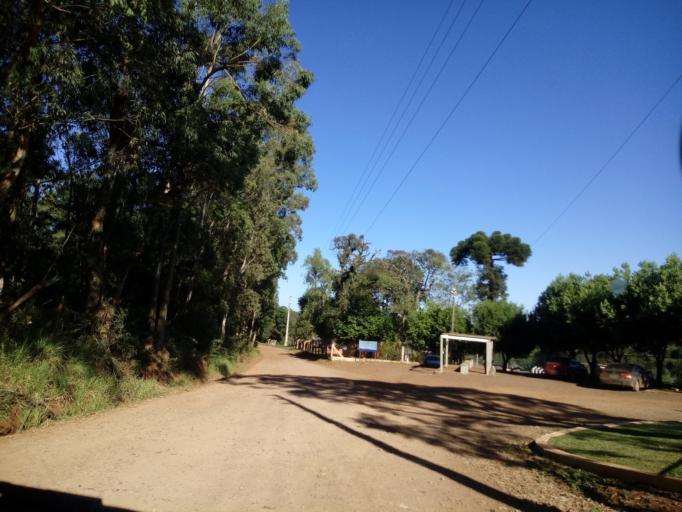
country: BR
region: Santa Catarina
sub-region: Chapeco
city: Chapeco
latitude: -27.2039
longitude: -52.6921
